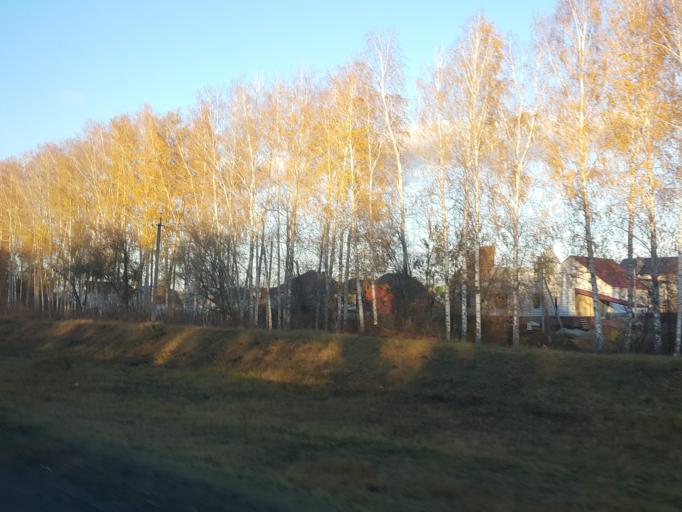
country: RU
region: Tambov
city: Bokino
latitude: 52.6200
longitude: 41.4439
